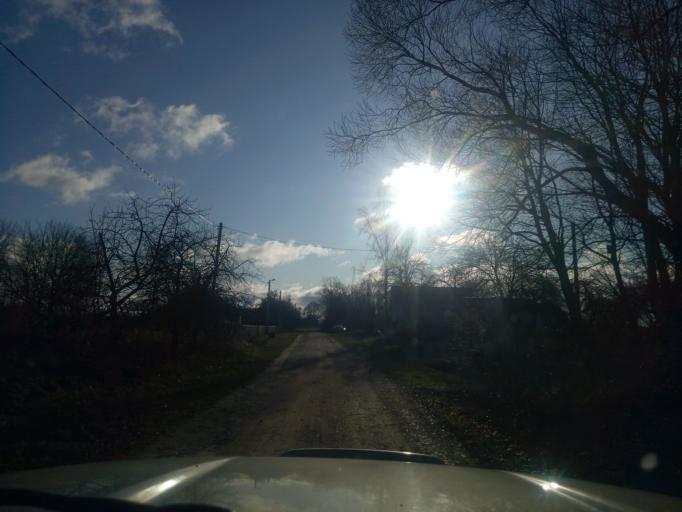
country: BY
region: Minsk
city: Tsimkavichy
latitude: 53.1770
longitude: 26.9086
